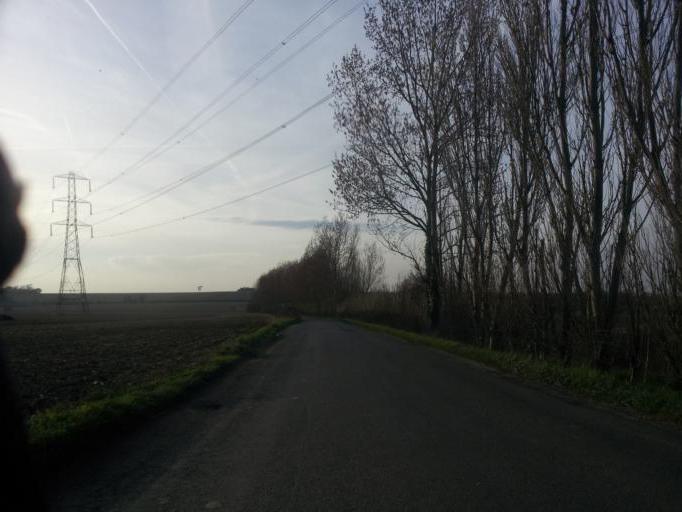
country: GB
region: England
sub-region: Kent
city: Sittingbourne
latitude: 51.3646
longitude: 0.7056
